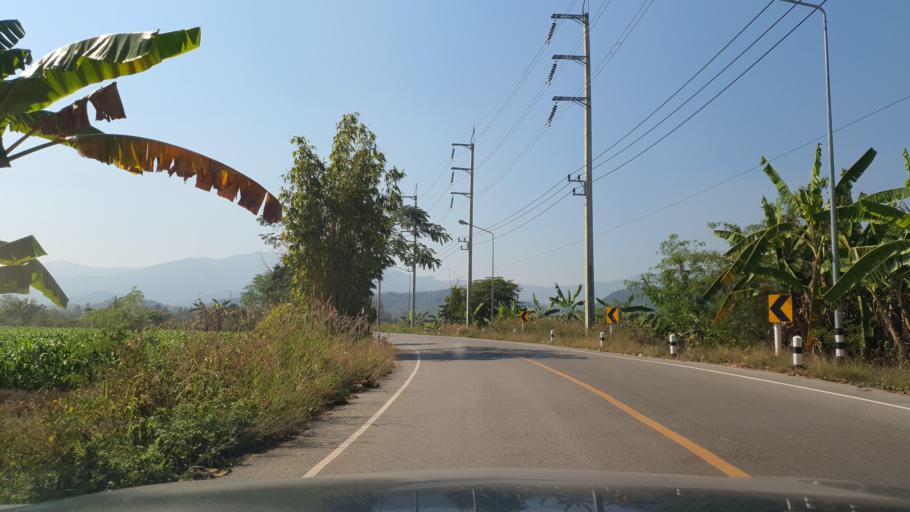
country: TH
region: Chiang Rai
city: Mae Lao
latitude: 19.8044
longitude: 99.6877
